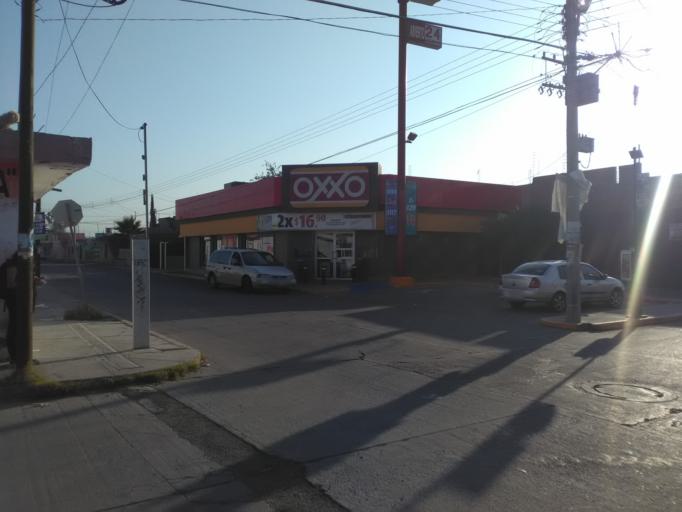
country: MX
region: Durango
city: Victoria de Durango
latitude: 24.0396
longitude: -104.6456
